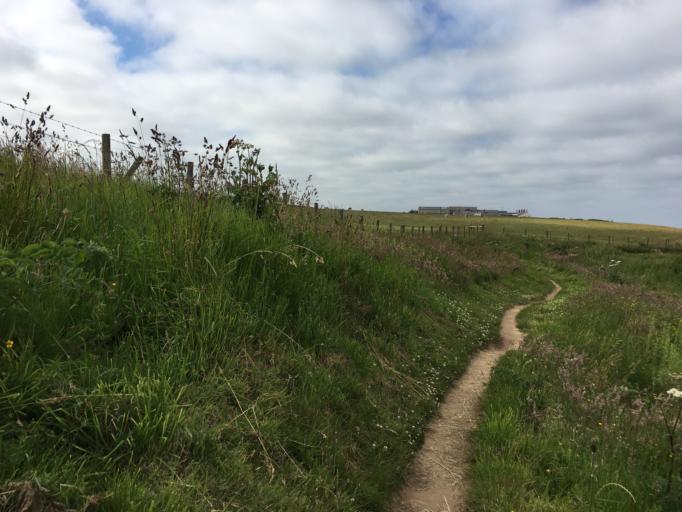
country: GB
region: England
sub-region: Northumberland
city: Alnmouth
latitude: 55.4445
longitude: -1.5903
